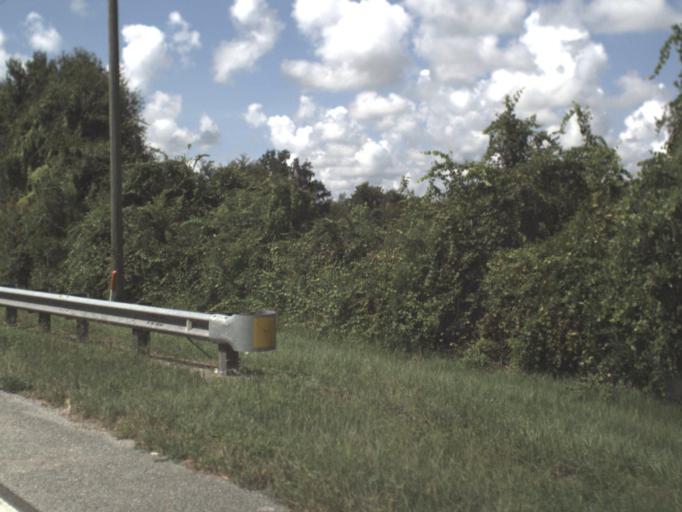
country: US
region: Florida
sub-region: DeSoto County
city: Arcadia
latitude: 27.3428
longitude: -81.8047
